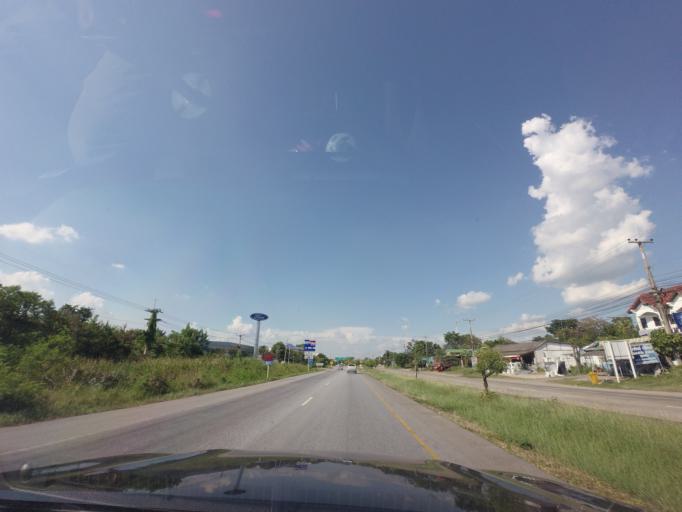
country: TH
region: Nakhon Ratchasima
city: Sida
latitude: 15.5432
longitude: 102.5470
